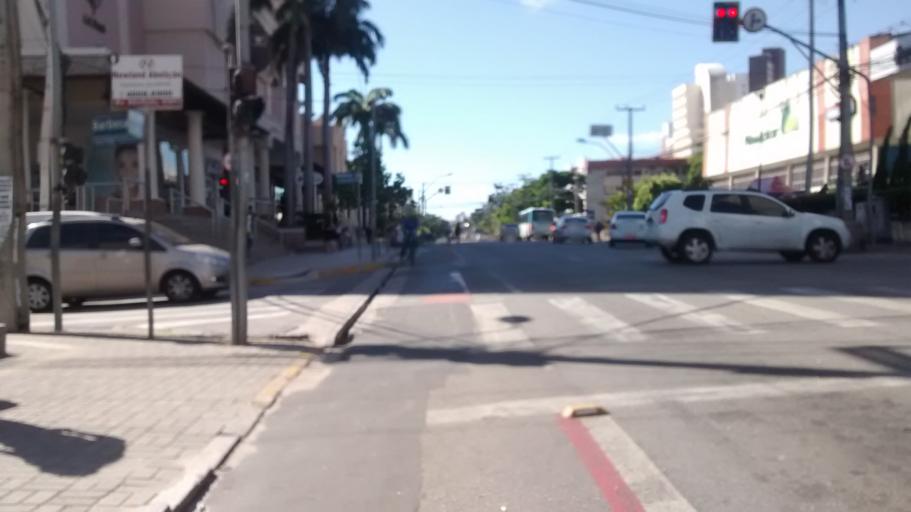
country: BR
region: Ceara
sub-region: Fortaleza
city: Fortaleza
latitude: -3.7365
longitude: -38.4975
